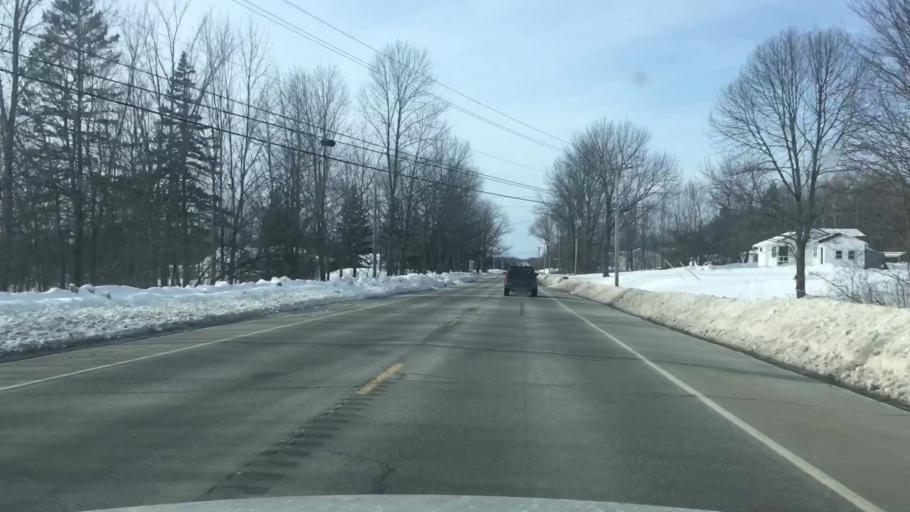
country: US
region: Maine
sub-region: Penobscot County
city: Kenduskeag
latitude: 44.9730
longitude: -68.9810
